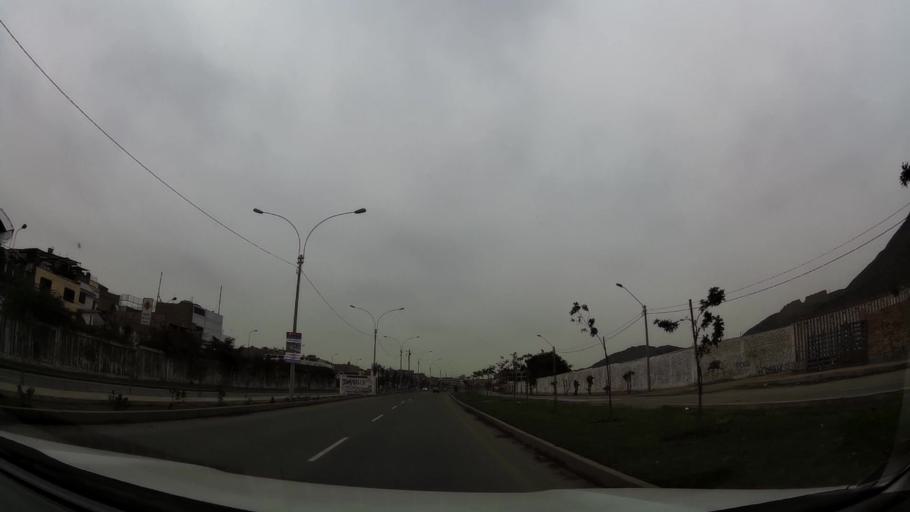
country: PE
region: Lima
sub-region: Lima
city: Vitarte
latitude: -12.0492
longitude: -76.9371
